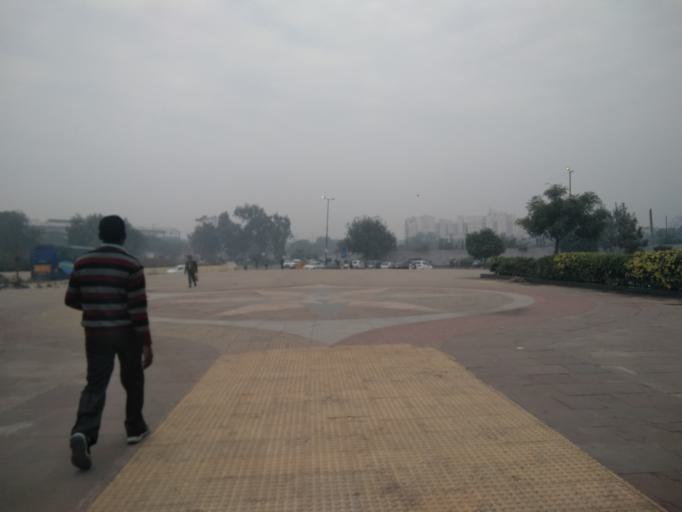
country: IN
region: Uttar Pradesh
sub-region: Gautam Buddha Nagar
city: Noida
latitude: 28.5382
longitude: 77.2865
